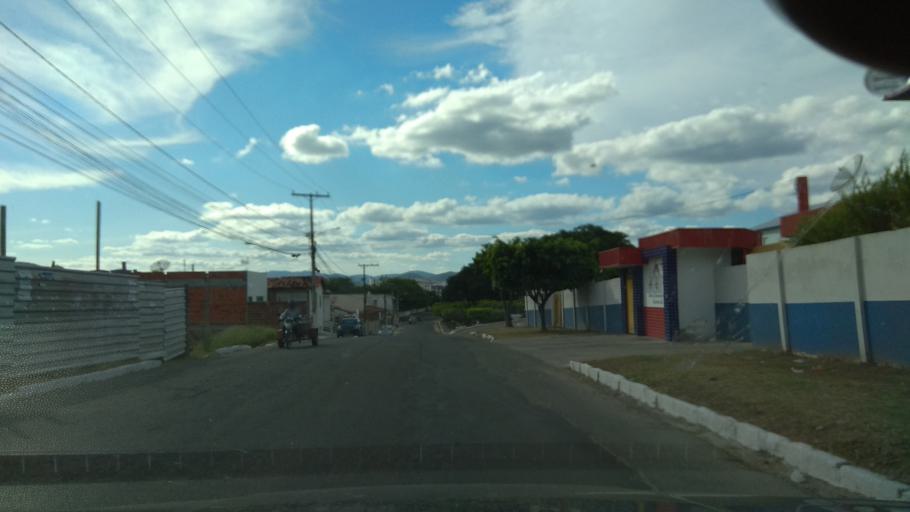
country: BR
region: Bahia
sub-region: Jequie
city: Jequie
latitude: -13.8739
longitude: -40.0747
